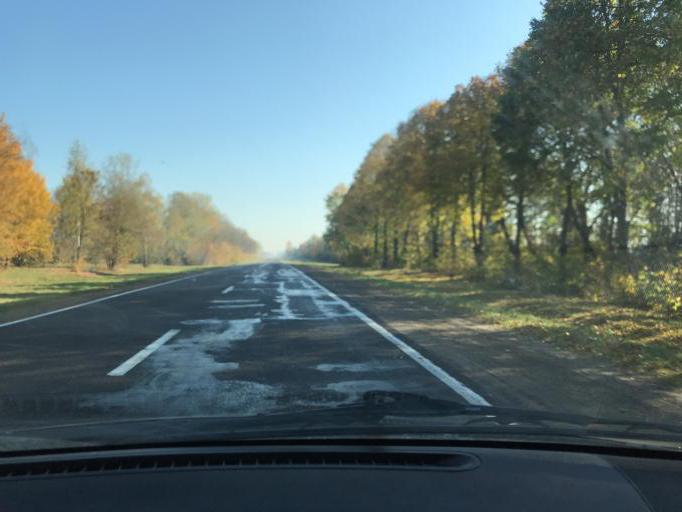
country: BY
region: Minsk
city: Klyetsk
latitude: 52.9648
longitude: 26.5109
